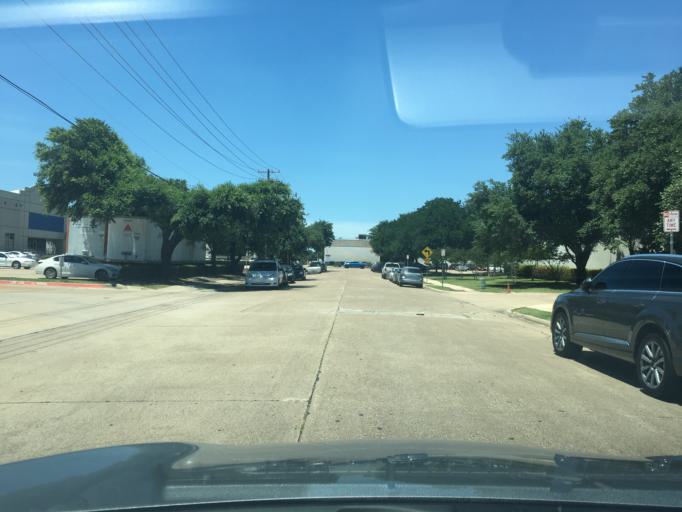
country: US
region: Texas
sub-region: Dallas County
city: Richardson
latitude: 32.9647
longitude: -96.7031
